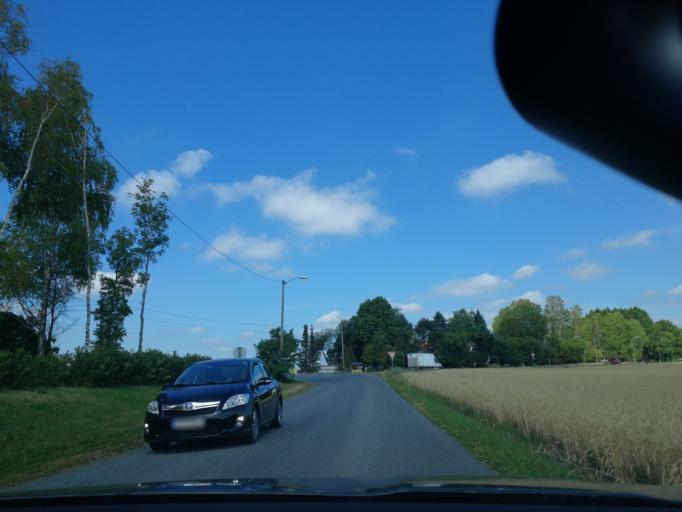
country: NO
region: Vestfold
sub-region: Sandefjord
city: Sandefjord
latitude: 59.1553
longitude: 10.2002
